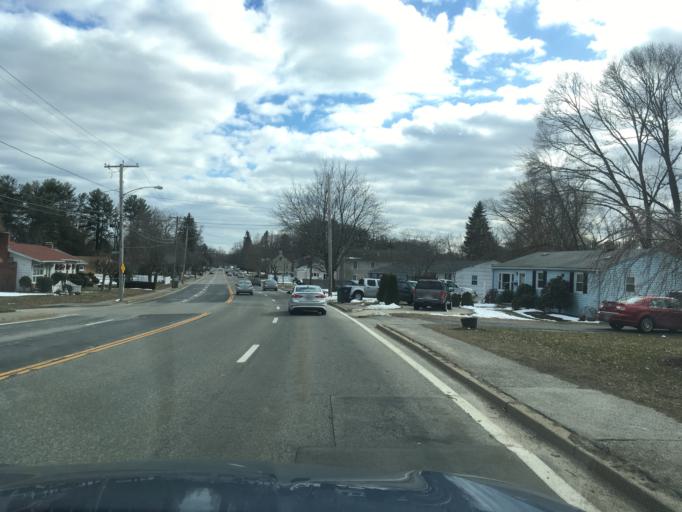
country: US
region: Rhode Island
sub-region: Kent County
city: Warwick
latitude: 41.7105
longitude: -71.4645
